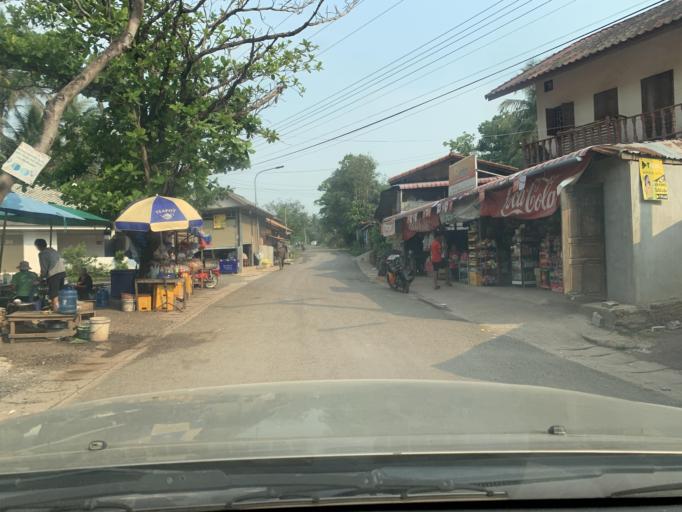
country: LA
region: Louangphabang
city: Louangphabang
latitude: 19.8966
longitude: 102.1279
